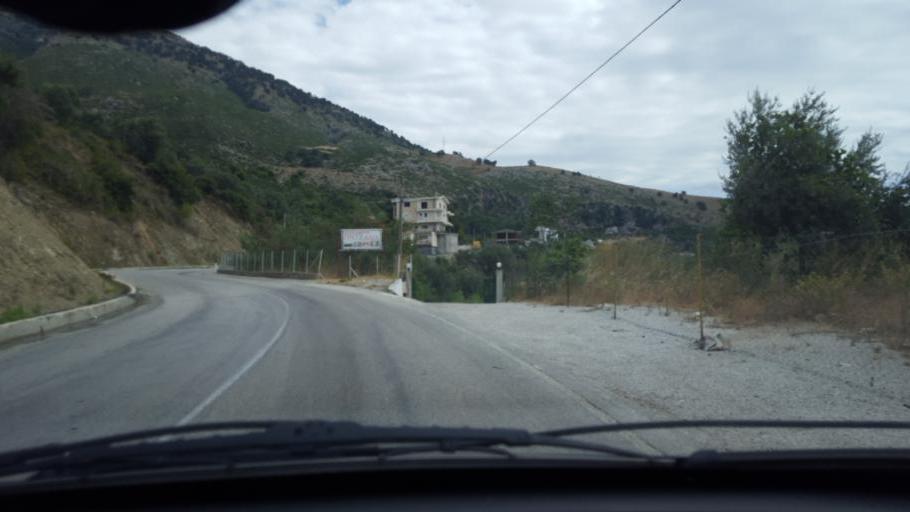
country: AL
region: Vlore
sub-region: Rrethi i Sarandes
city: Lukove
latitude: 40.0557
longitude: 19.8649
